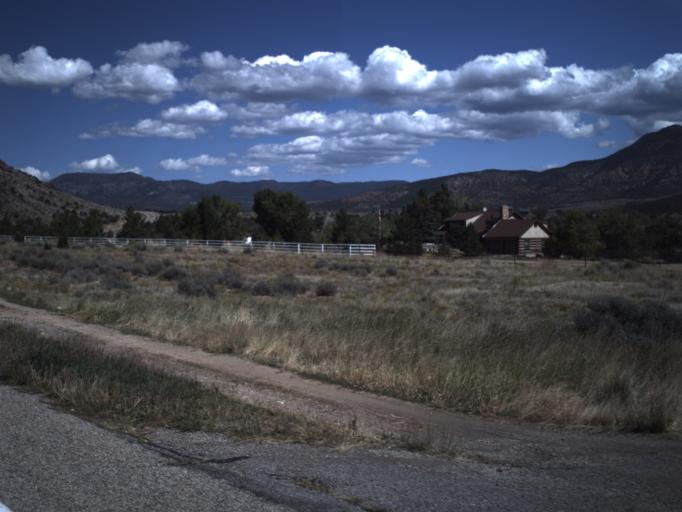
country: US
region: Utah
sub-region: Washington County
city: Ivins
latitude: 37.3671
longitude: -113.6668
